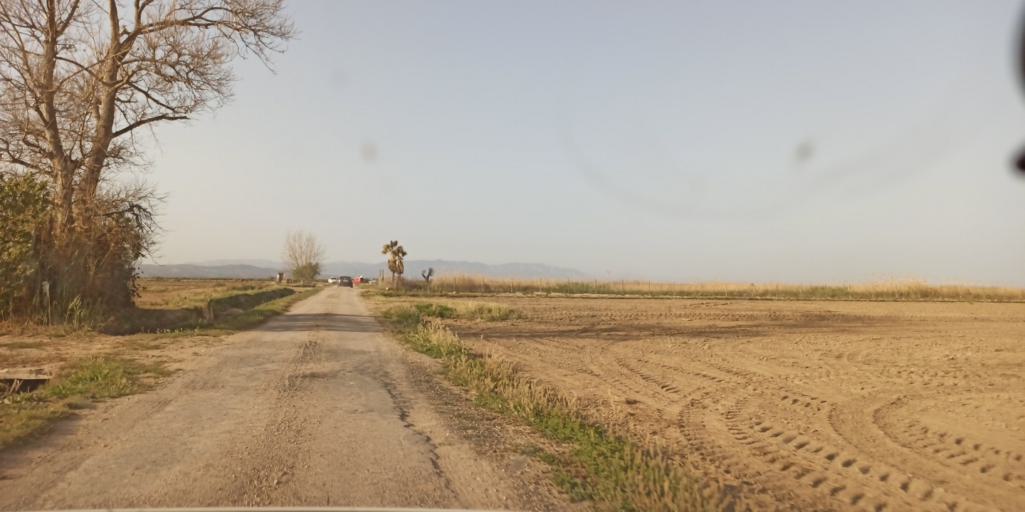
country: ES
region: Catalonia
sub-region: Provincia de Tarragona
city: Deltebre
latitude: 40.7608
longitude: 0.7543
